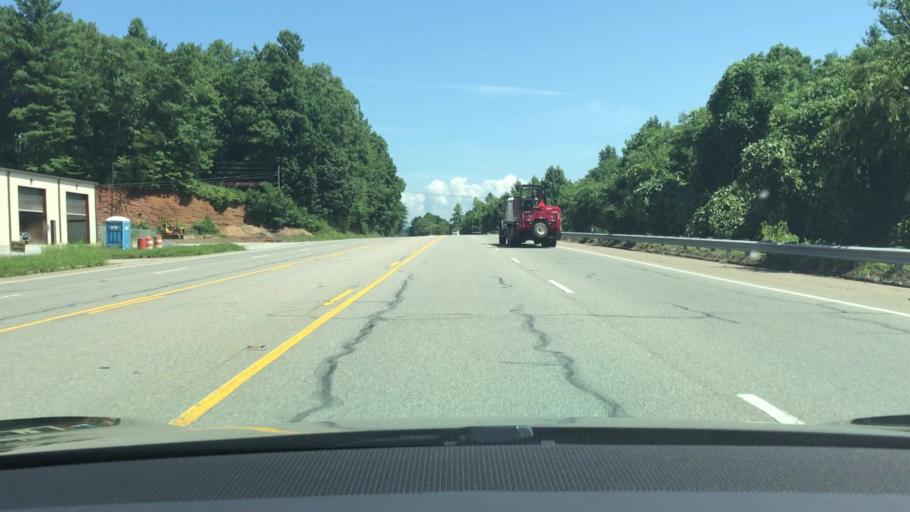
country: US
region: North Carolina
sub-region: Macon County
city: Franklin
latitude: 35.0881
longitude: -83.3836
